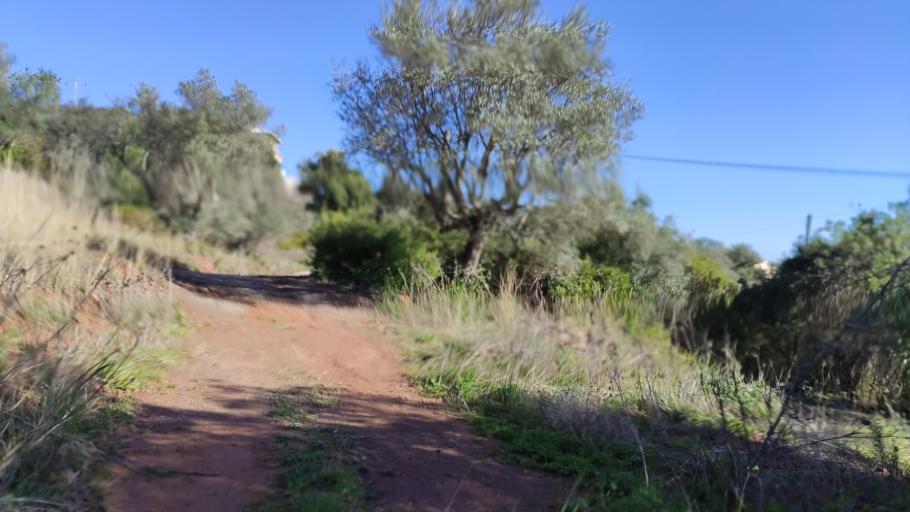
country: PT
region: Faro
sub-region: Sao Bras de Alportel
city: Sao Bras de Alportel
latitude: 37.1561
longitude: -7.9092
